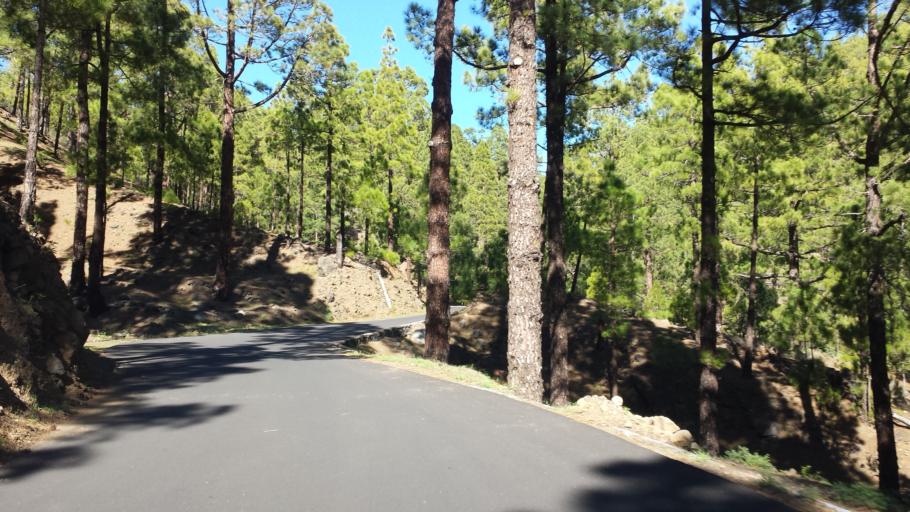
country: ES
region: Canary Islands
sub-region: Provincia de Santa Cruz de Tenerife
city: El Paso
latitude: 28.6955
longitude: -17.8545
